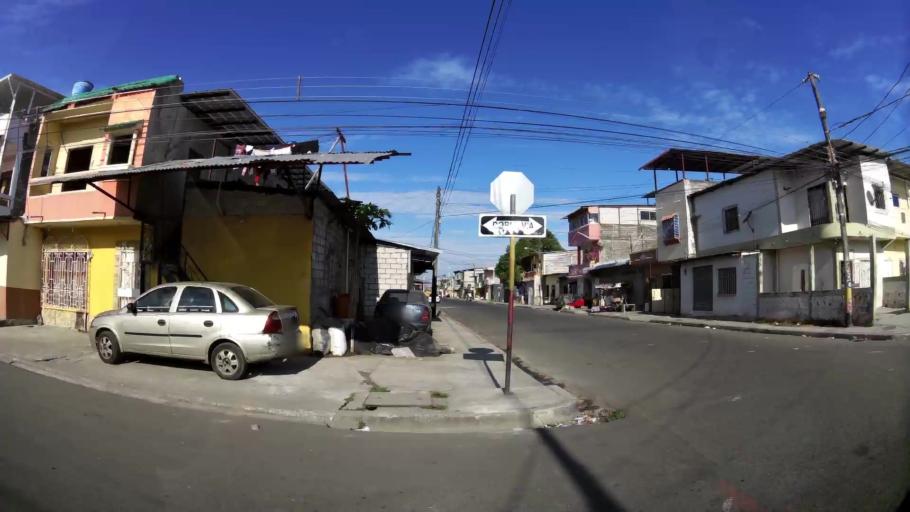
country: EC
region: Guayas
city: Guayaquil
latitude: -2.2237
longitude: -79.9310
